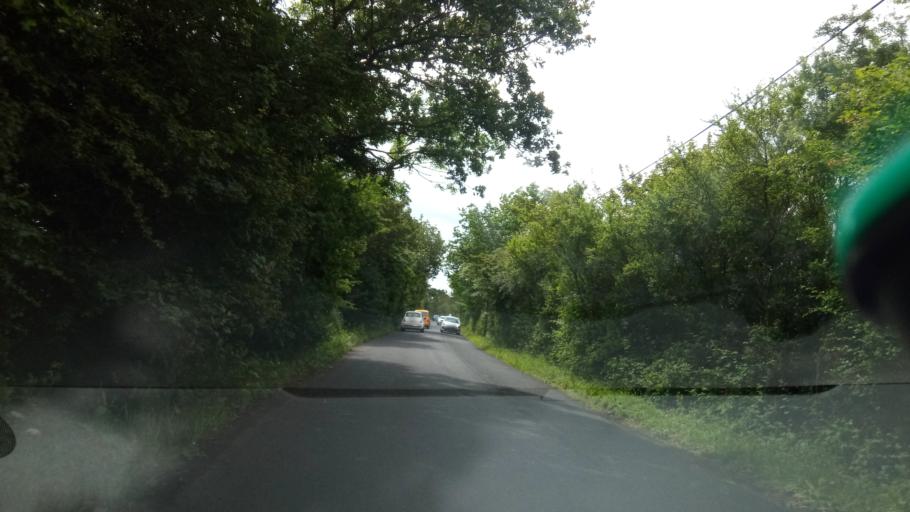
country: GB
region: England
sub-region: Derbyshire
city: Findern
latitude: 52.8619
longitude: -1.5298
